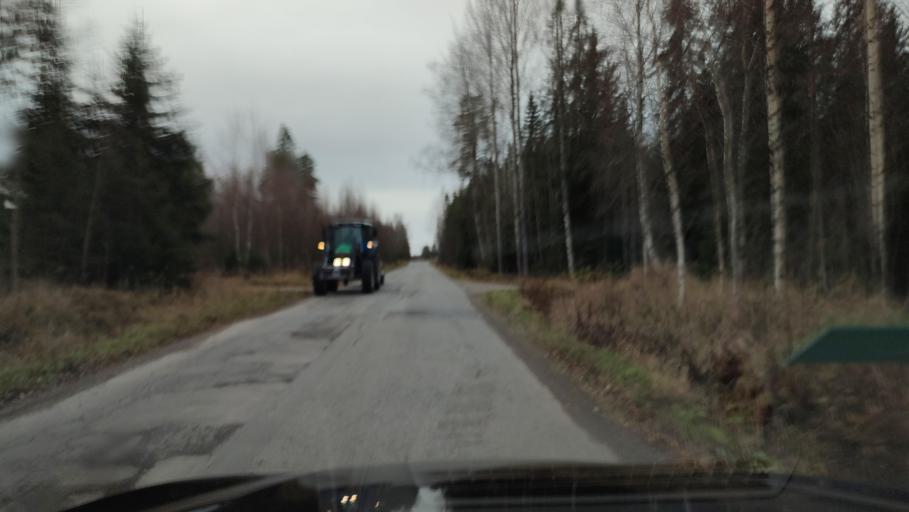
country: FI
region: Ostrobothnia
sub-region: Sydosterbotten
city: Naerpes
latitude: 62.4250
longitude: 21.4139
